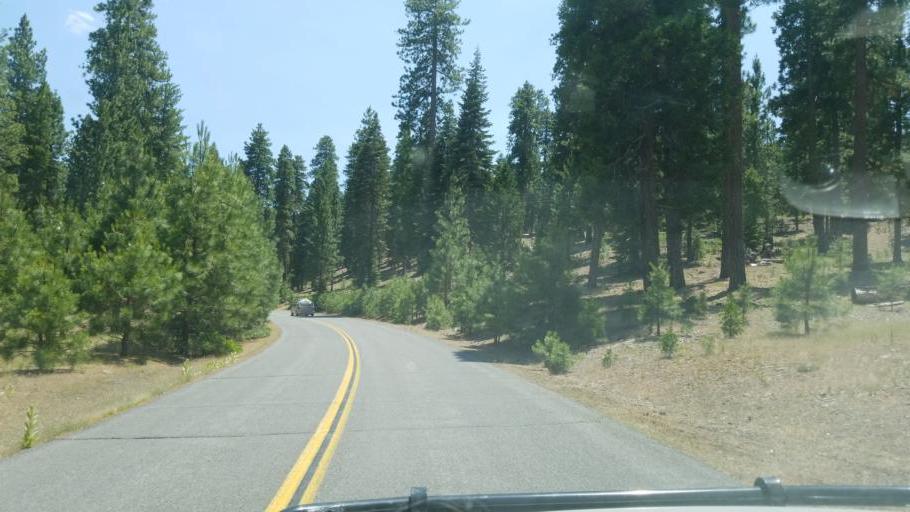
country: US
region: California
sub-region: Lassen County
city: Susanville
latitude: 40.5565
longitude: -120.8265
